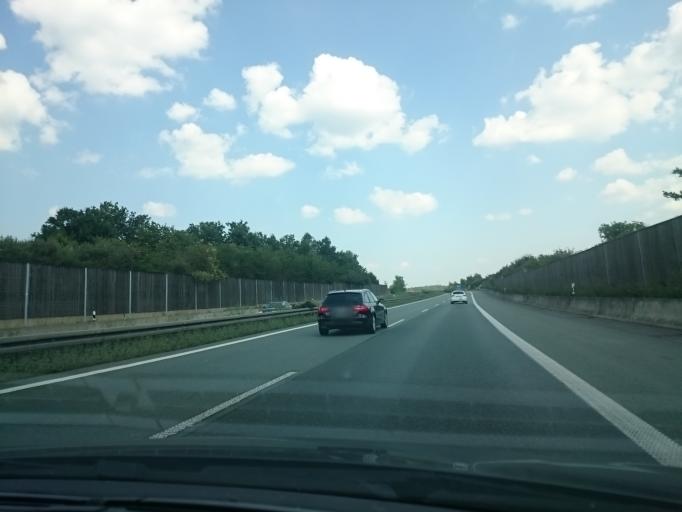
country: DE
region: Saxony
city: Limbach
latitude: 50.5398
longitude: 12.2577
